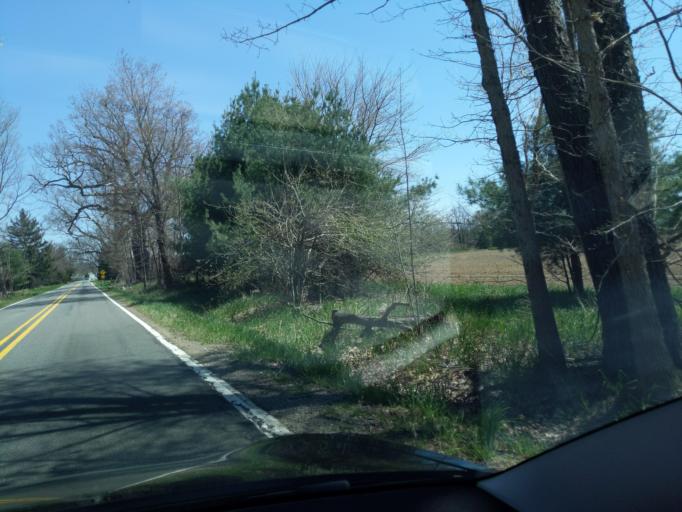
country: US
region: Michigan
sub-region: Ingham County
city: Stockbridge
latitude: 42.5012
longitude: -84.2337
